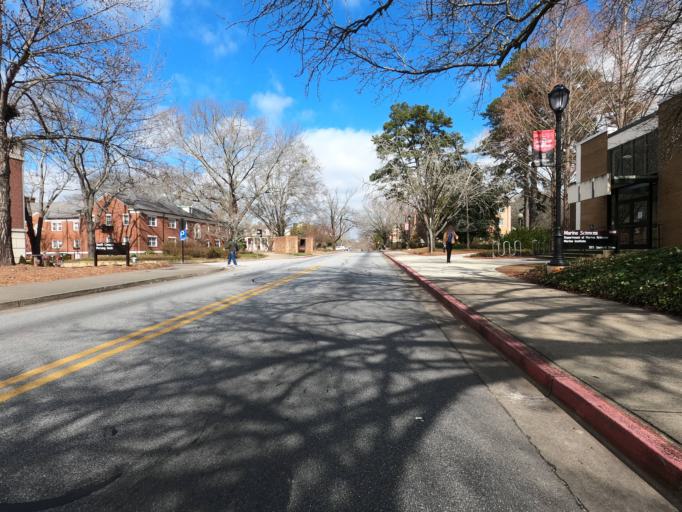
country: US
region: Georgia
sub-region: Clarke County
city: Athens
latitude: 33.9453
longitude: -83.3766
